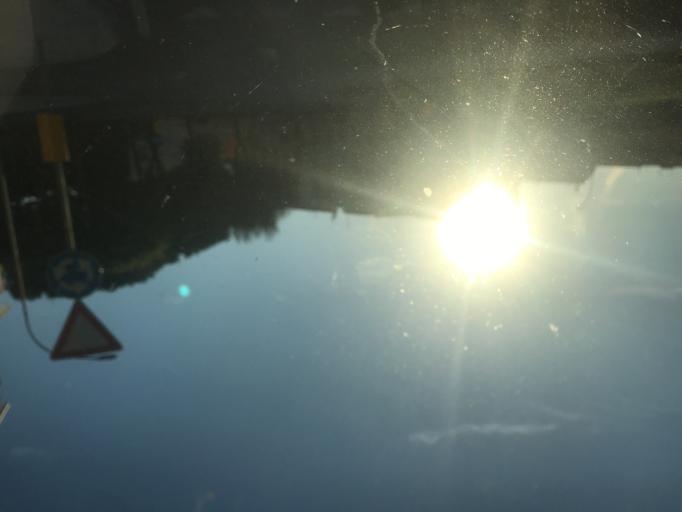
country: IT
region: Sardinia
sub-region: Provincia di Sassari
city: Alghero
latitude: 40.5727
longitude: 8.3228
